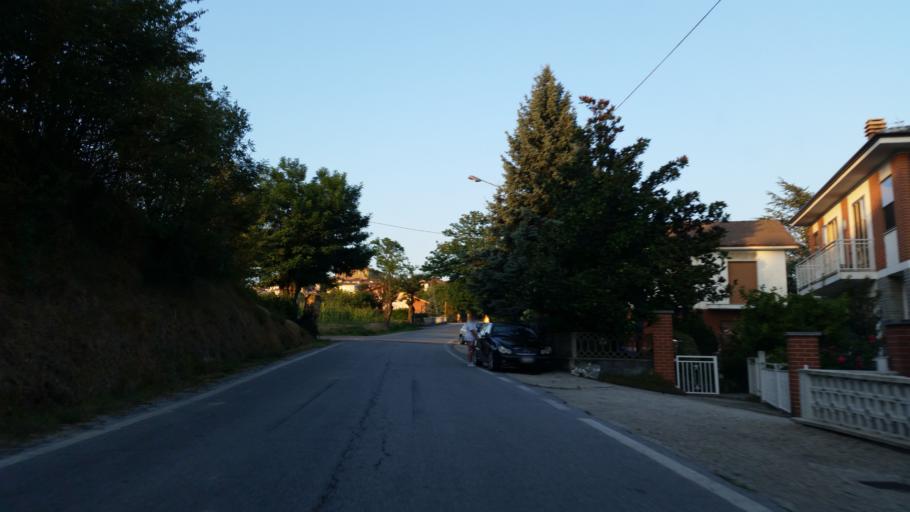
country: IT
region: Piedmont
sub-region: Provincia di Cuneo
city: Mango
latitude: 44.6818
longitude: 8.1446
